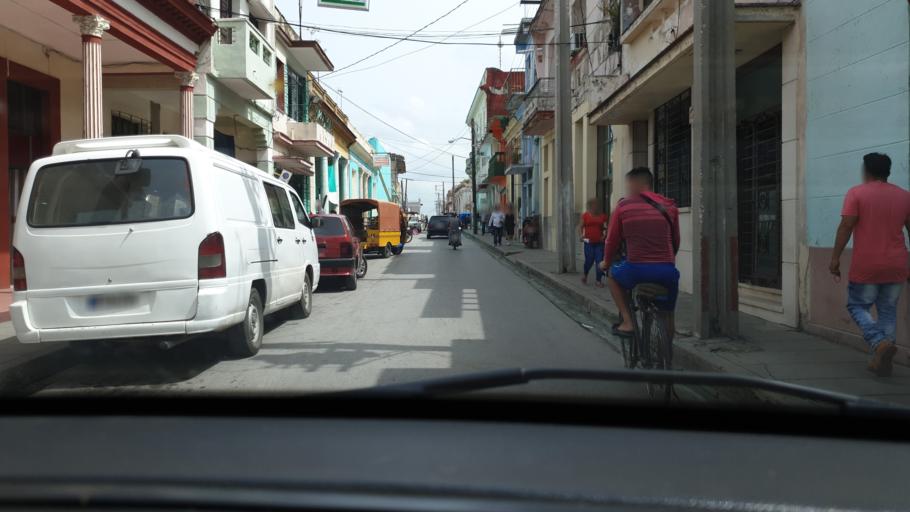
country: CU
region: Villa Clara
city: Santa Clara
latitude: 22.4061
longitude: -79.9668
